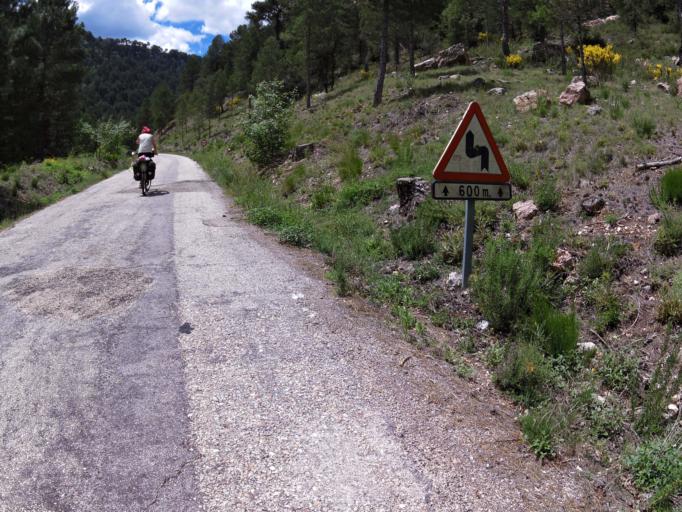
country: ES
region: Castille-La Mancha
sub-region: Provincia de Albacete
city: Paterna del Madera
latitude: 38.5725
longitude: -2.3567
